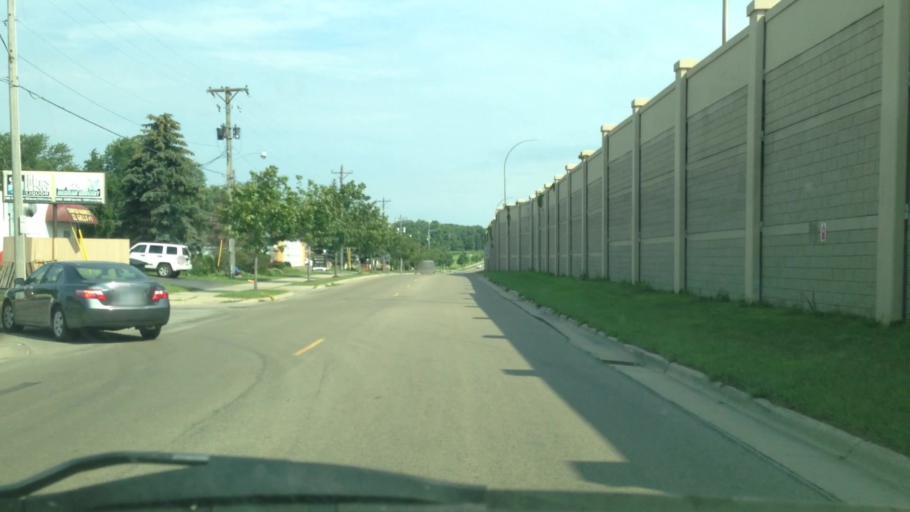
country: US
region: Minnesota
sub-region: Olmsted County
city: Rochester
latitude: 44.0478
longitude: -92.4908
